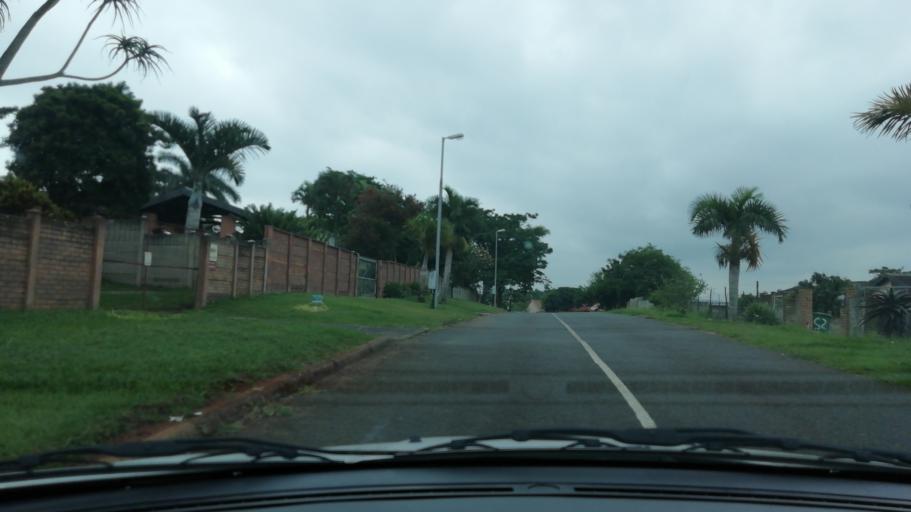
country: ZA
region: KwaZulu-Natal
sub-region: uThungulu District Municipality
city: Empangeni
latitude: -28.7350
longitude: 31.9018
